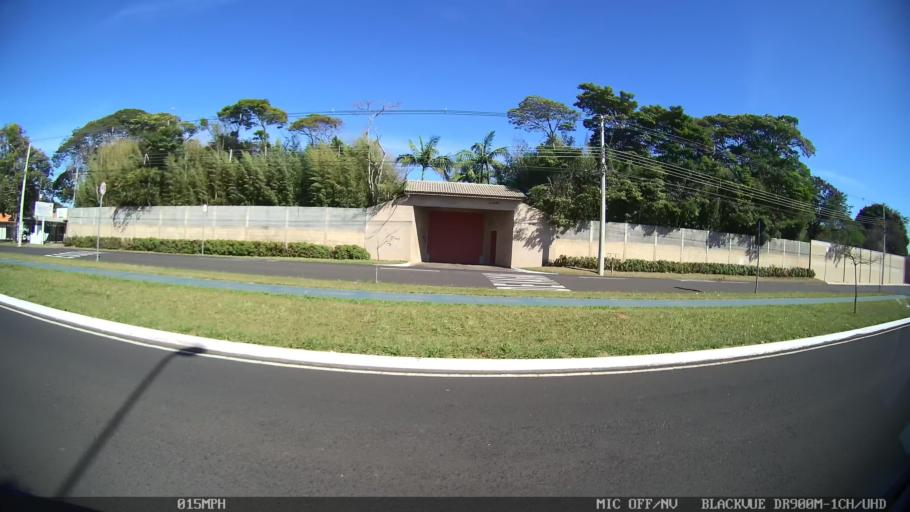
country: BR
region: Sao Paulo
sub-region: Franca
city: Franca
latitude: -20.5598
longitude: -47.3593
